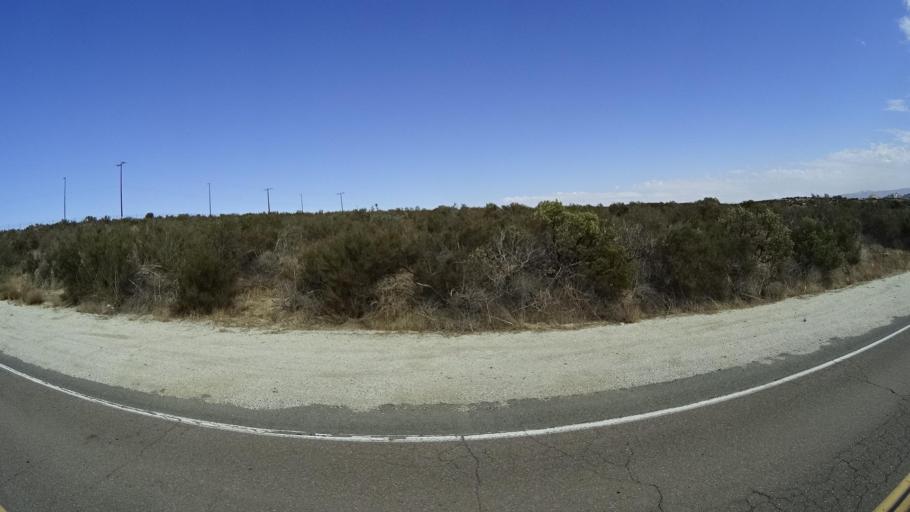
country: US
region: California
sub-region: San Diego County
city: Campo
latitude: 32.6797
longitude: -116.2922
